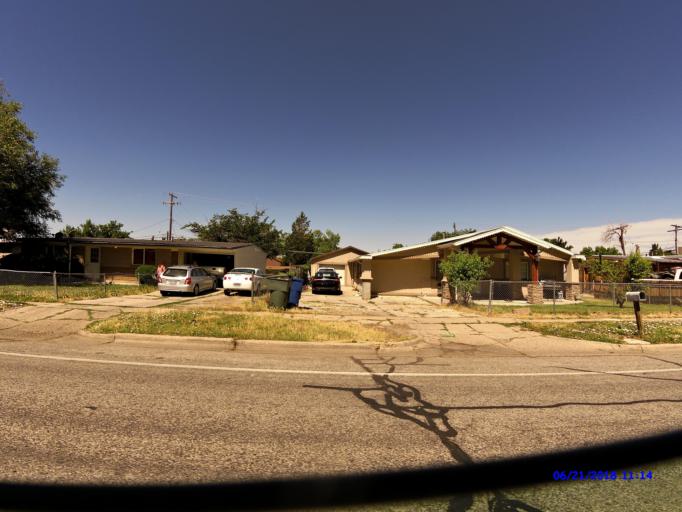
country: US
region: Utah
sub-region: Weber County
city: Harrisville
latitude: 41.2739
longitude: -111.9592
